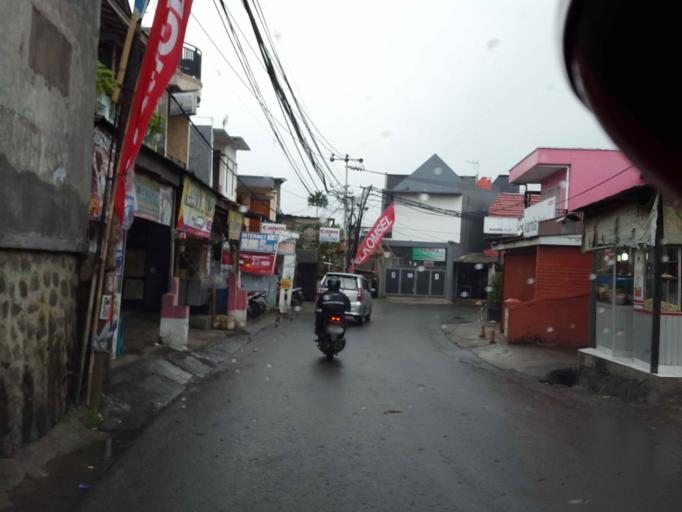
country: ID
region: West Java
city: Cimahi
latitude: -6.8657
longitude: 107.5745
